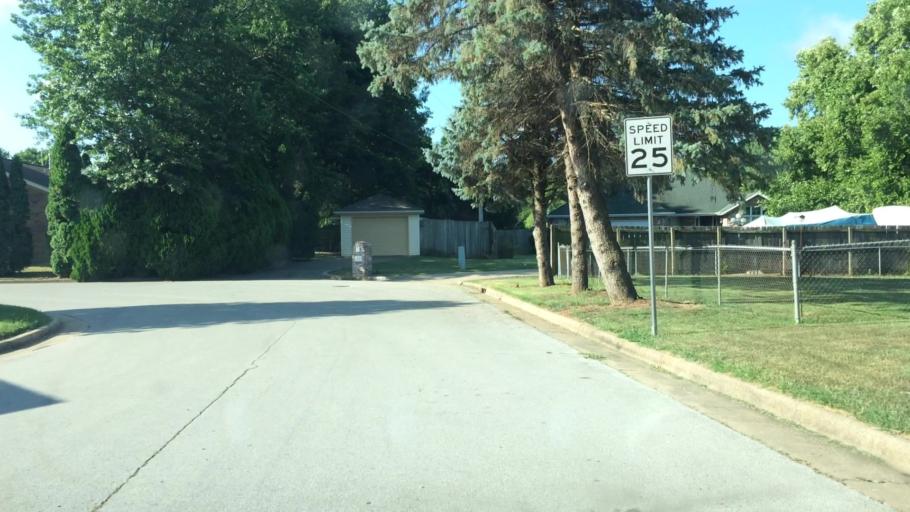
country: US
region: Missouri
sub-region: Greene County
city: Springfield
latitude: 37.2585
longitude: -93.2719
